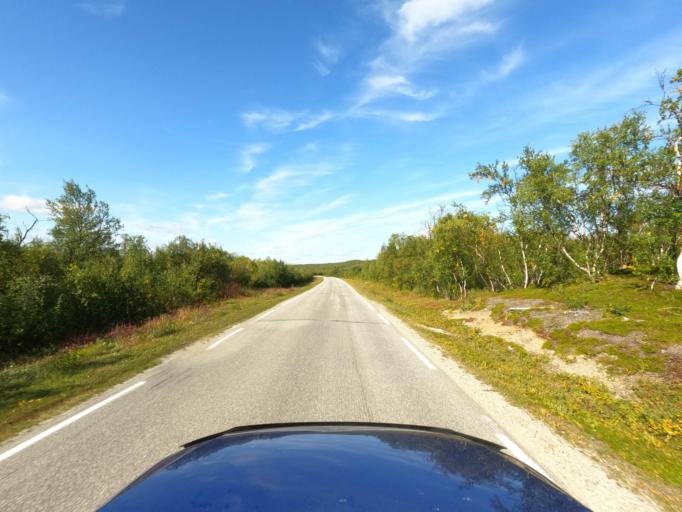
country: NO
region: Finnmark Fylke
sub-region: Porsanger
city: Lakselv
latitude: 69.7569
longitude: 25.2124
